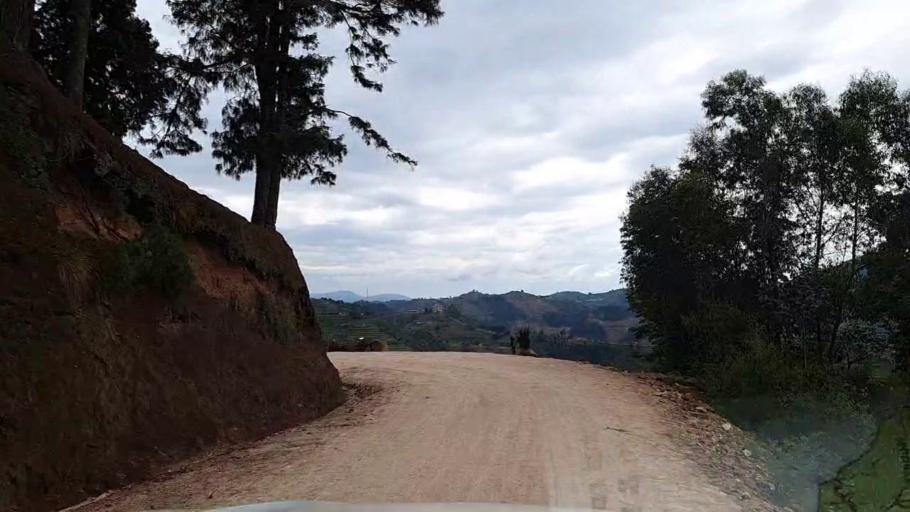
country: RW
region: Southern Province
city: Nzega
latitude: -2.4059
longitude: 29.4539
